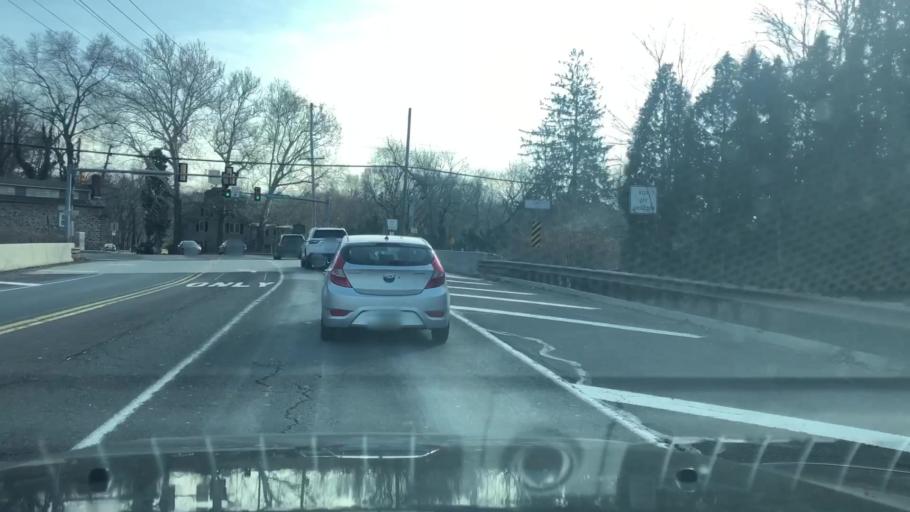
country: US
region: Pennsylvania
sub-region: Bucks County
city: Langhorne
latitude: 40.1910
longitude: -74.9271
